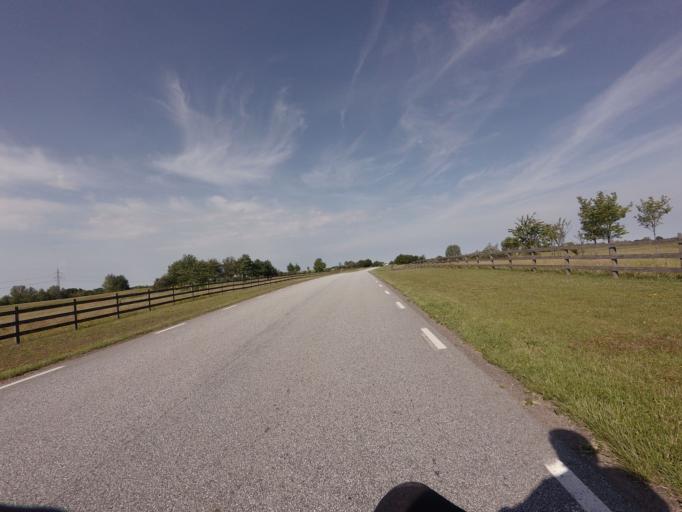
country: SE
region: Skane
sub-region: Malmo
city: Oxie
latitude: 55.4938
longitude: 13.0971
